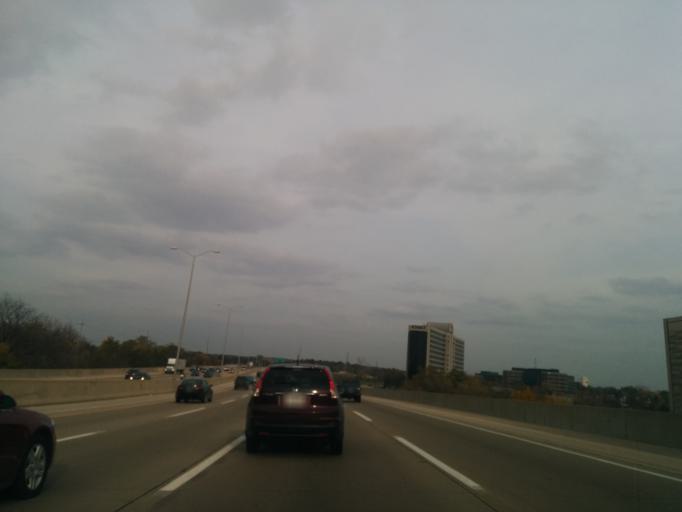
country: US
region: Illinois
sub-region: DuPage County
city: Lisle
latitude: 41.8063
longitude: -88.0834
